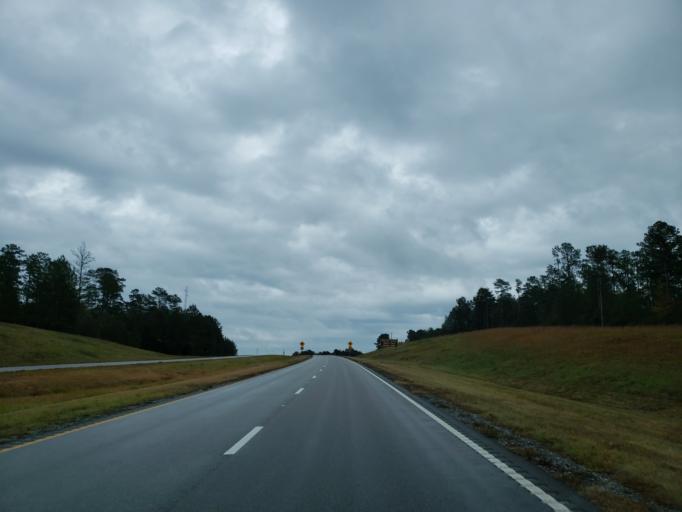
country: US
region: Mississippi
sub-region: Wayne County
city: Waynesboro
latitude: 31.6844
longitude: -88.6984
